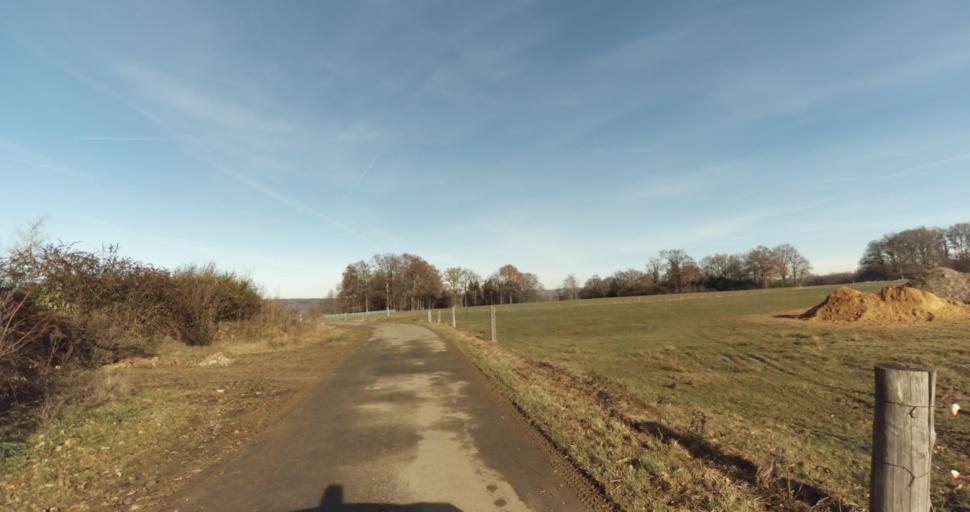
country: FR
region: Limousin
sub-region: Departement de la Haute-Vienne
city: Sereilhac
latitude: 45.7804
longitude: 1.0917
